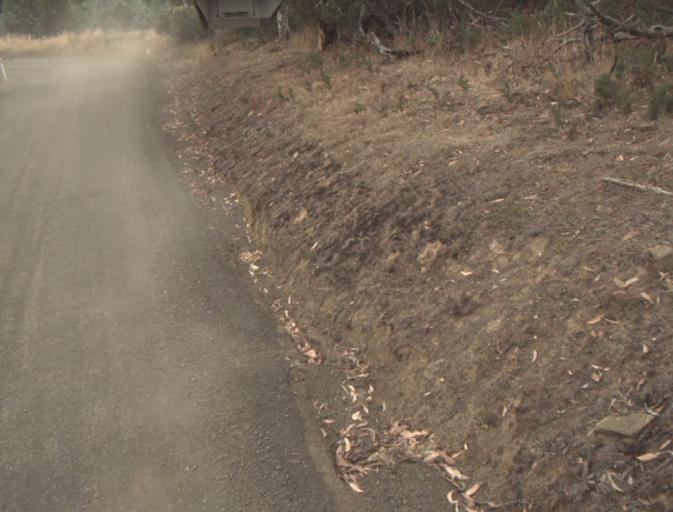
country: AU
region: Tasmania
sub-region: Northern Midlands
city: Evandale
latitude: -41.4802
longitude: 147.5354
